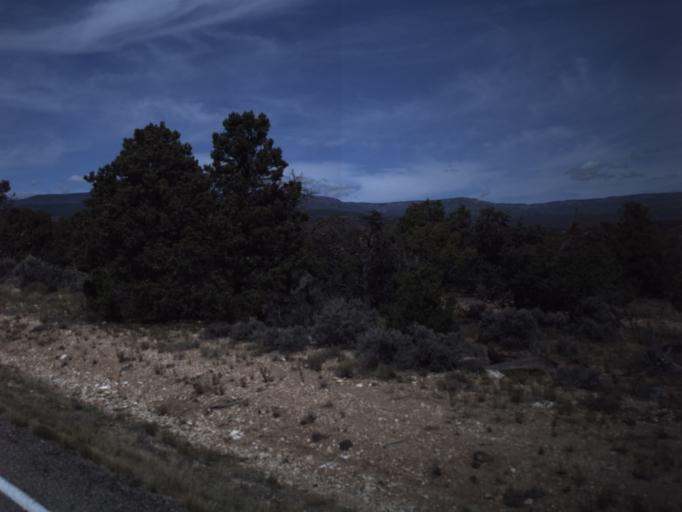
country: US
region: Utah
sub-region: Wayne County
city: Loa
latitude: 37.8784
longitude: -111.4551
